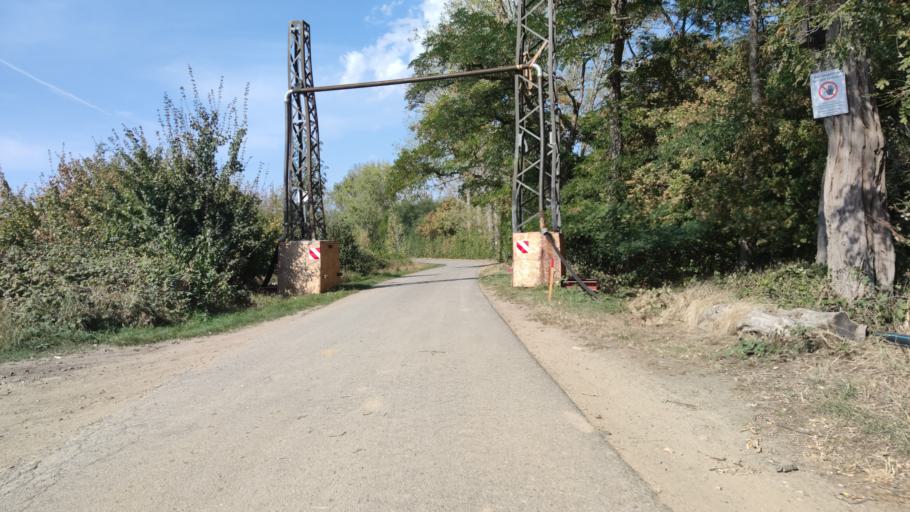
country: DE
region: North Rhine-Westphalia
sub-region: Regierungsbezirk Koln
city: Inden
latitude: 50.8366
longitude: 6.3820
